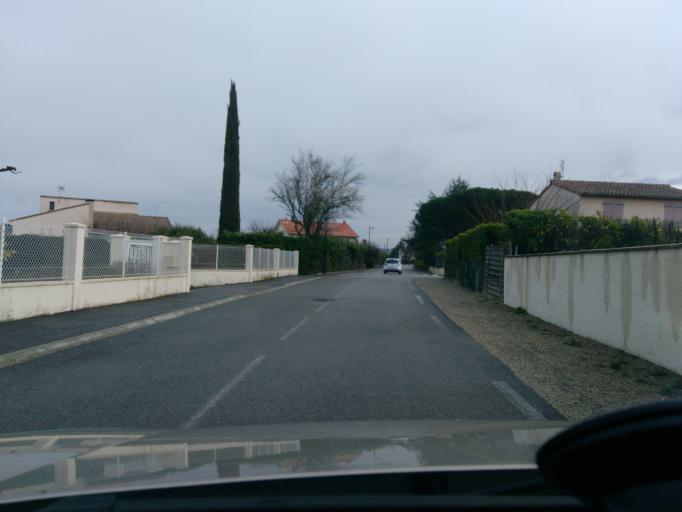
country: FR
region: Rhone-Alpes
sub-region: Departement de la Drome
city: Montelimar
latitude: 44.5351
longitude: 4.7564
